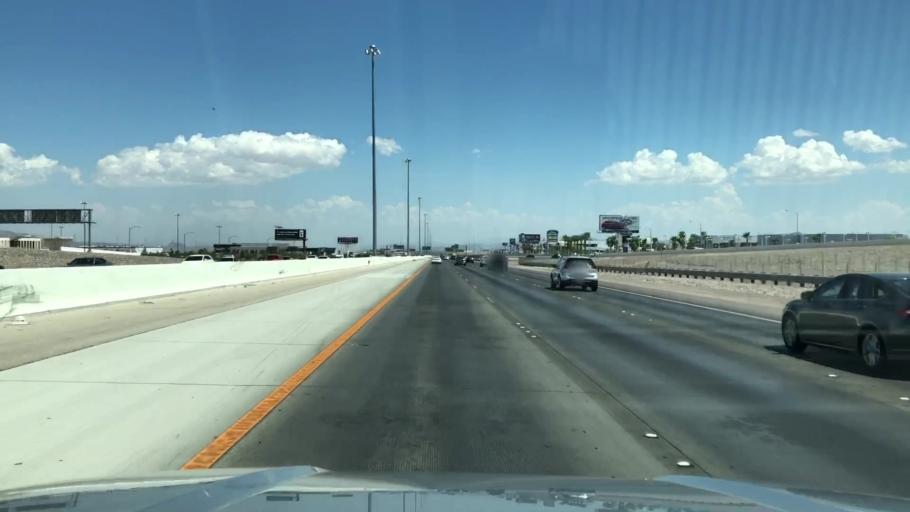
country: US
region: Nevada
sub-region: Clark County
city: Enterprise
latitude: 36.0666
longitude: -115.2414
